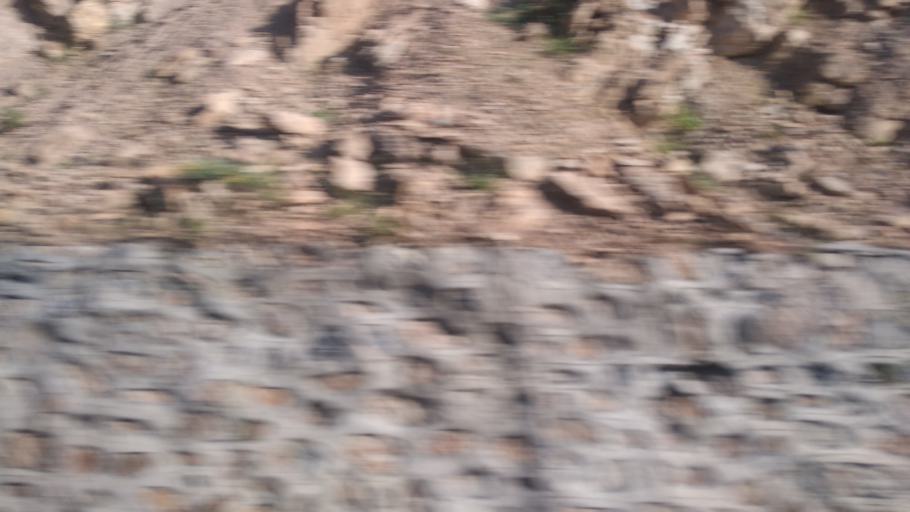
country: TR
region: Bitlis
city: Resadiye
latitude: 38.4761
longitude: 42.5301
